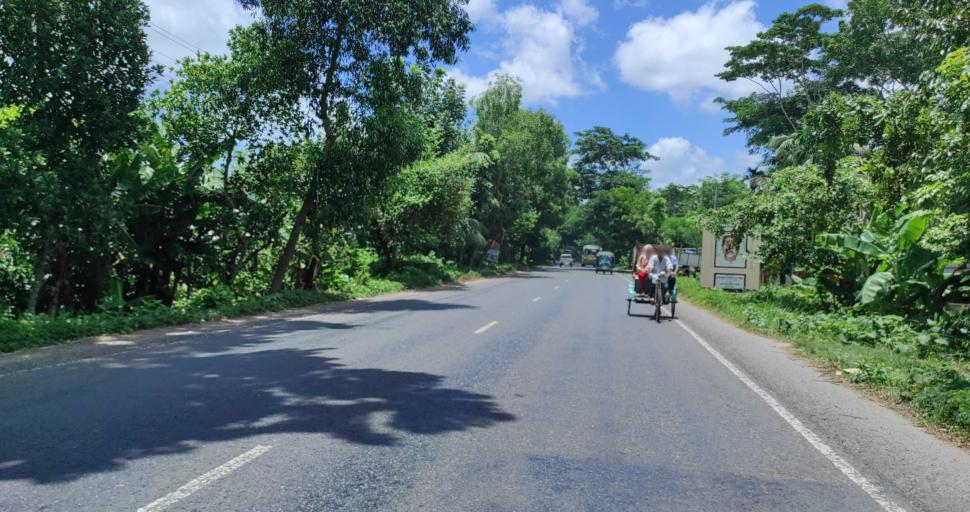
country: BD
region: Barisal
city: Gaurnadi
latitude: 22.8352
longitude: 90.2537
